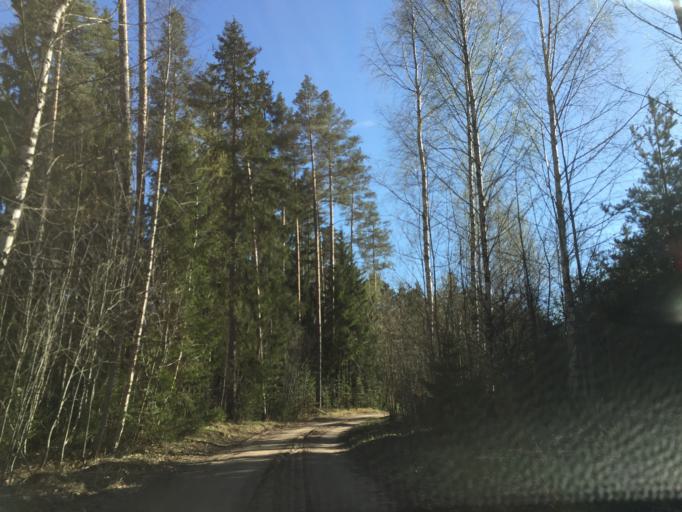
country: EE
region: Valgamaa
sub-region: Valga linn
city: Valga
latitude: 57.7833
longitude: 26.2446
